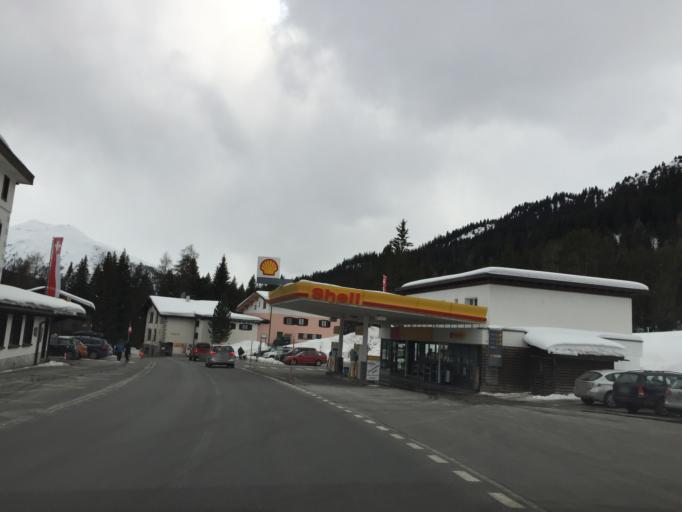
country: CH
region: Grisons
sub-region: Praettigau/Davos District
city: Davos
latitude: 46.8331
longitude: 9.8541
